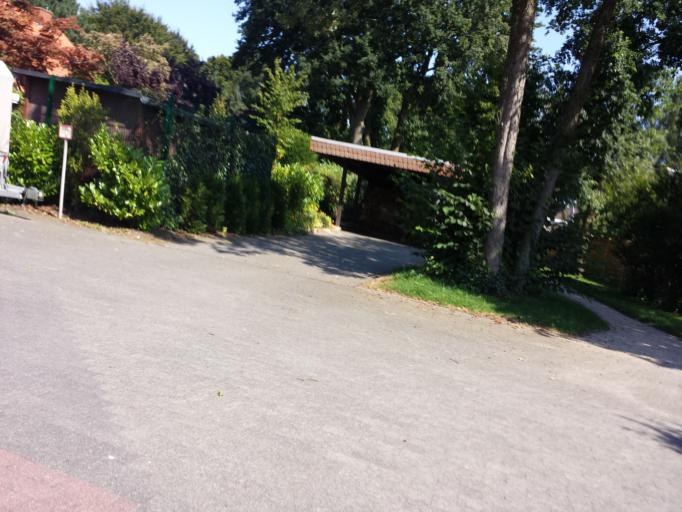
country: DE
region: North Rhine-Westphalia
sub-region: Regierungsbezirk Detmold
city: Guetersloh
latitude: 51.8807
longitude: 8.3826
